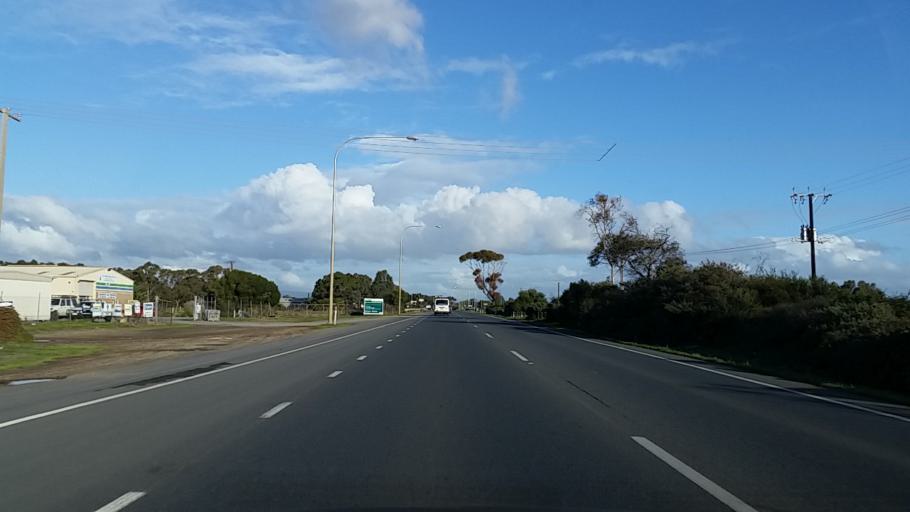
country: AU
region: South Australia
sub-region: Salisbury
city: Salisbury
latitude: -34.7454
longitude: 138.5870
